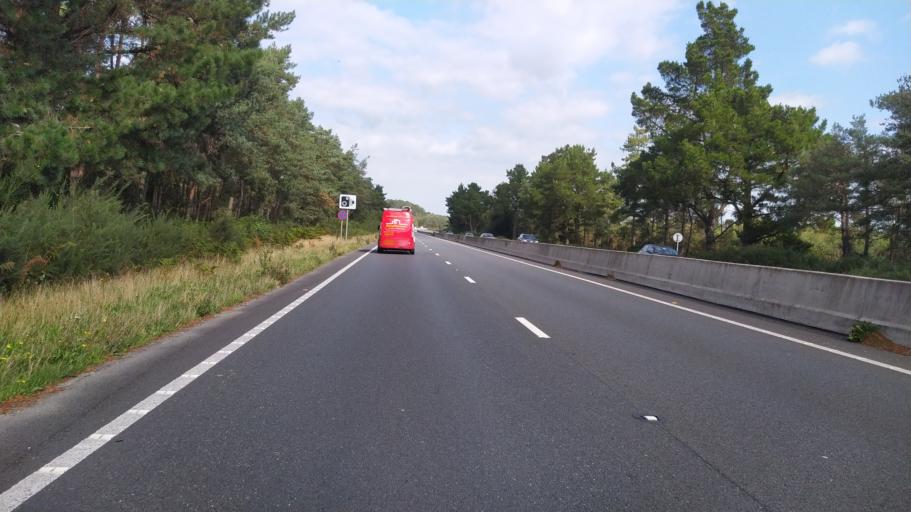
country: GB
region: England
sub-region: Dorset
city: St Leonards
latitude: 50.7937
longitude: -1.8151
